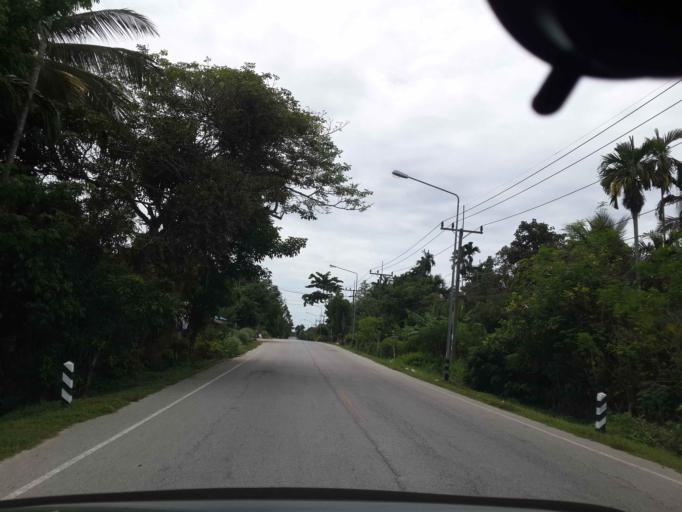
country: TH
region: Narathiwat
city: Yi-ngo
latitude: 6.3440
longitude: 101.6260
